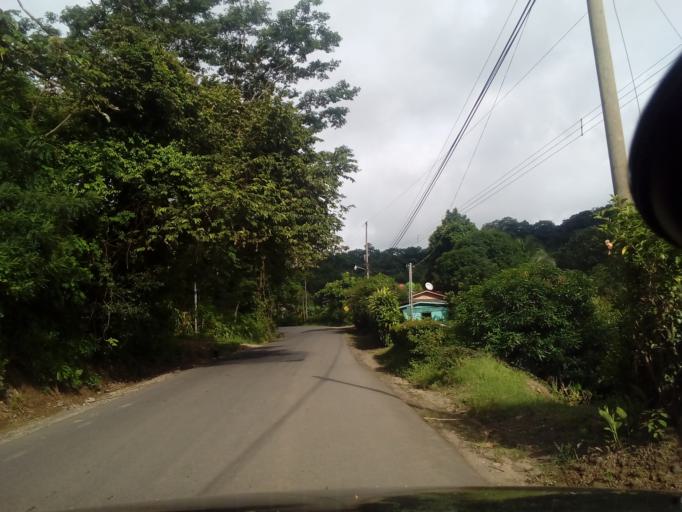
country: CR
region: Guanacaste
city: Samara
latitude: 9.9204
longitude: -85.5326
